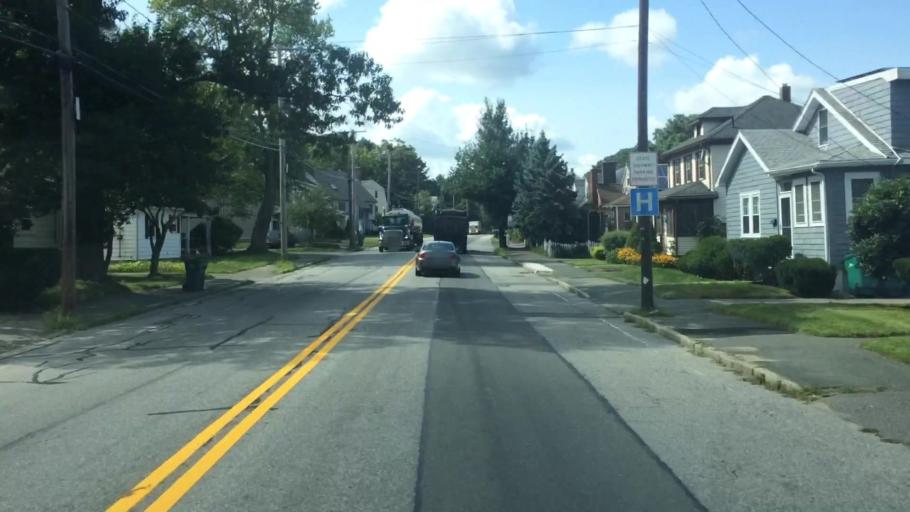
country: US
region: Massachusetts
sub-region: Essex County
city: South Peabody
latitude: 42.4984
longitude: -70.9723
